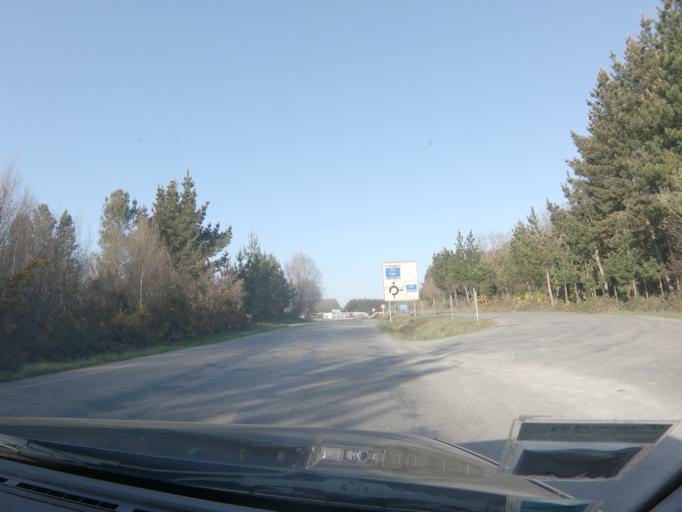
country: ES
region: Galicia
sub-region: Provincia de Lugo
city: Corgo
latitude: 42.9383
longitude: -7.3975
